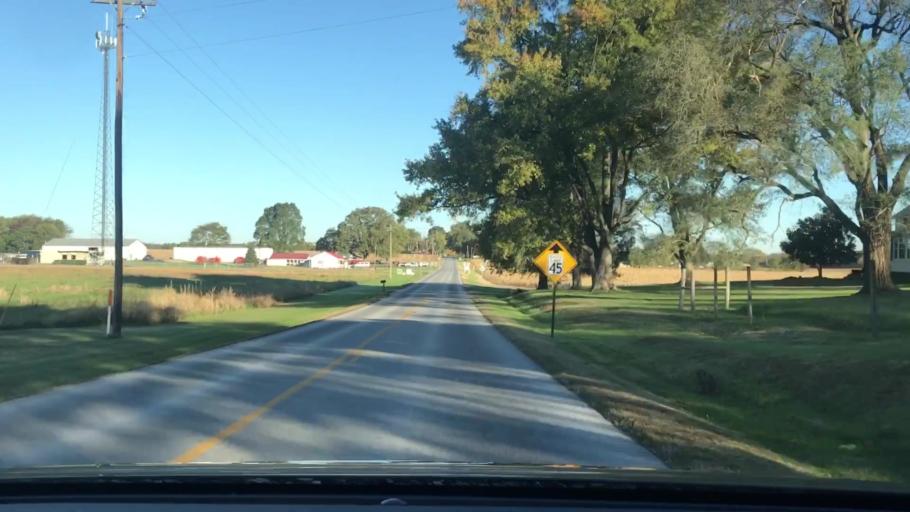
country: US
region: Kentucky
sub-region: Logan County
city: Auburn
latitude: 36.8495
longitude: -86.7051
